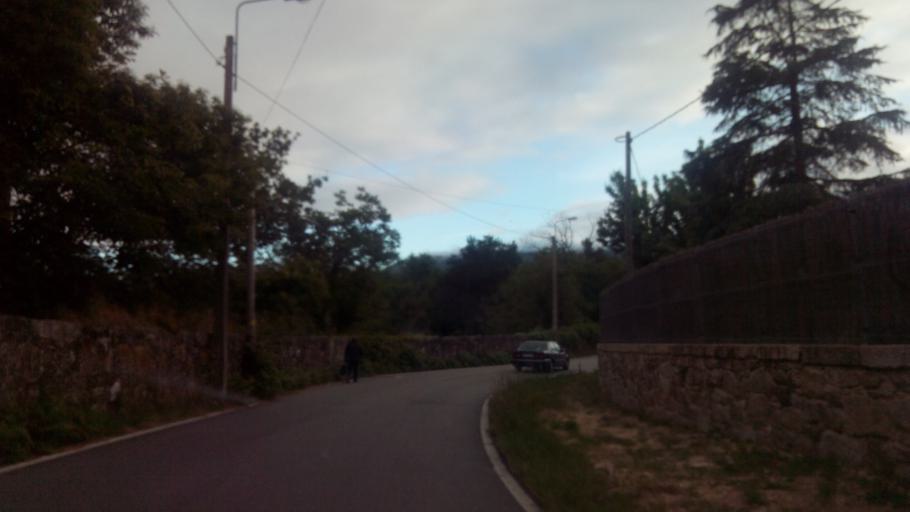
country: ES
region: Galicia
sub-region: Provincia de Pontevedra
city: Nigran
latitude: 42.1236
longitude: -8.8062
